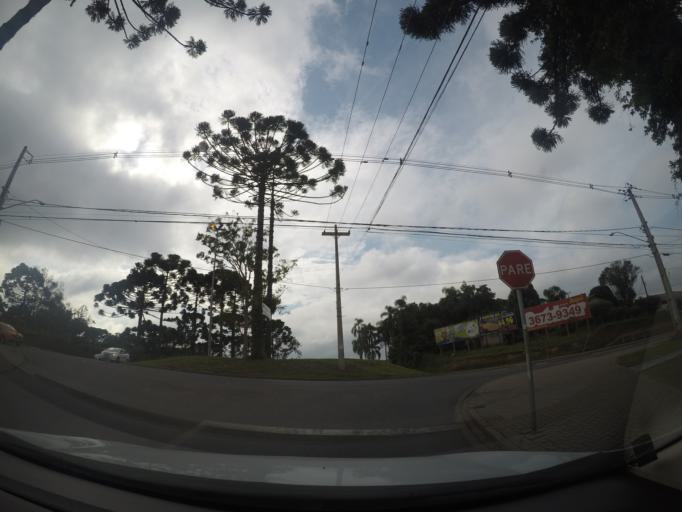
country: BR
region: Parana
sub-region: Colombo
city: Colombo
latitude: -25.3548
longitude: -49.2005
